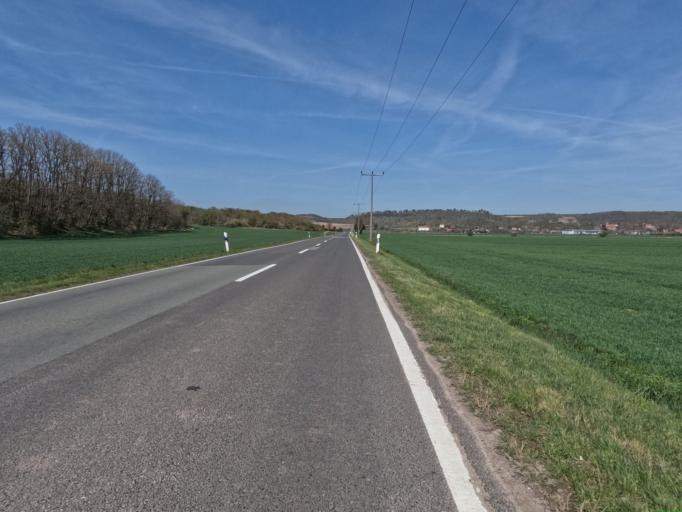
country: DE
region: Saxony-Anhalt
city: Beesenstedt
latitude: 51.6068
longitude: 11.7459
